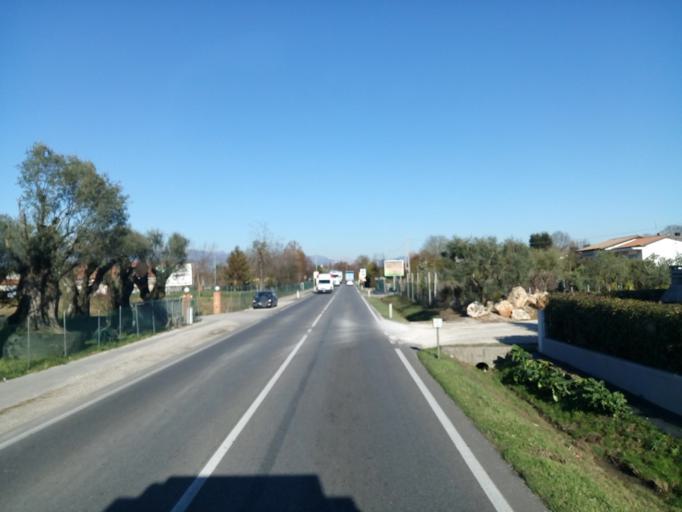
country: IT
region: Veneto
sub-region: Provincia di Treviso
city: Valla
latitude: 45.6931
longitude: 11.9276
